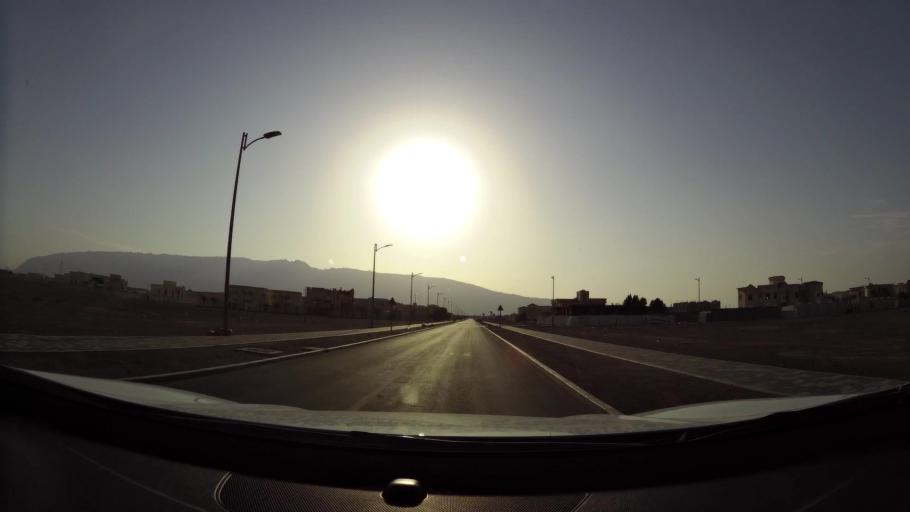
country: AE
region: Abu Dhabi
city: Al Ain
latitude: 24.0986
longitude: 55.8414
